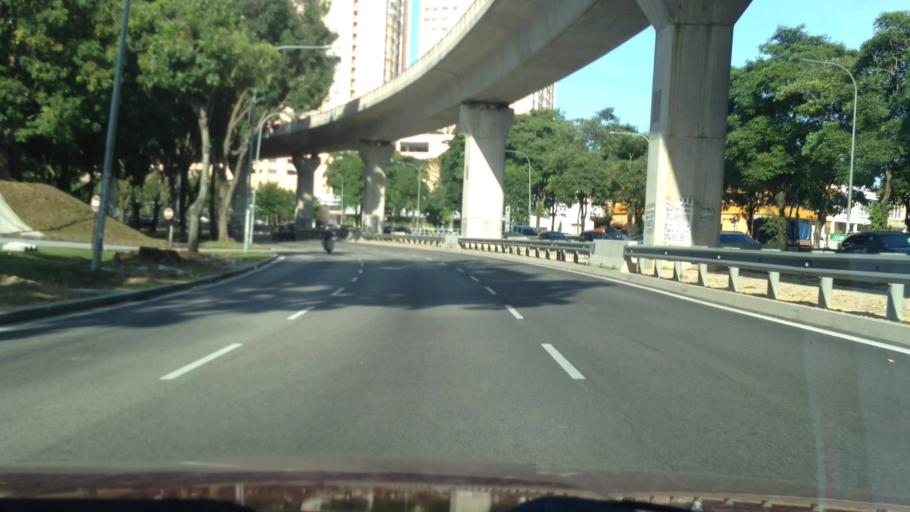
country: MY
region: Selangor
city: Subang Jaya
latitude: 3.0311
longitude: 101.5864
